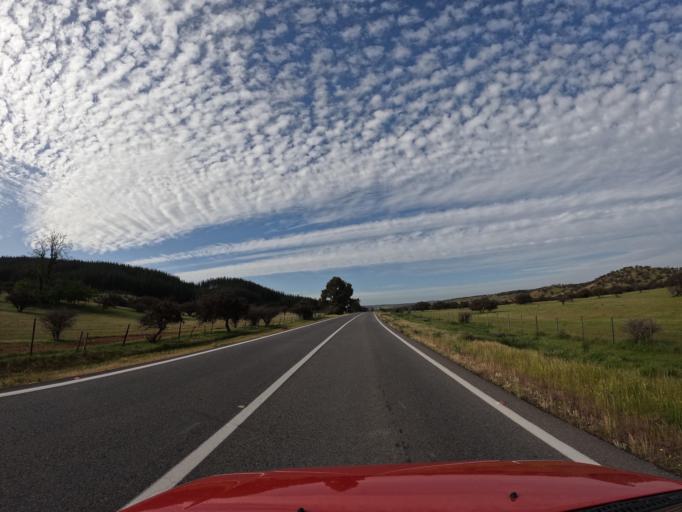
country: CL
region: O'Higgins
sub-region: Provincia de Colchagua
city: Santa Cruz
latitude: -34.3053
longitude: -71.7363
